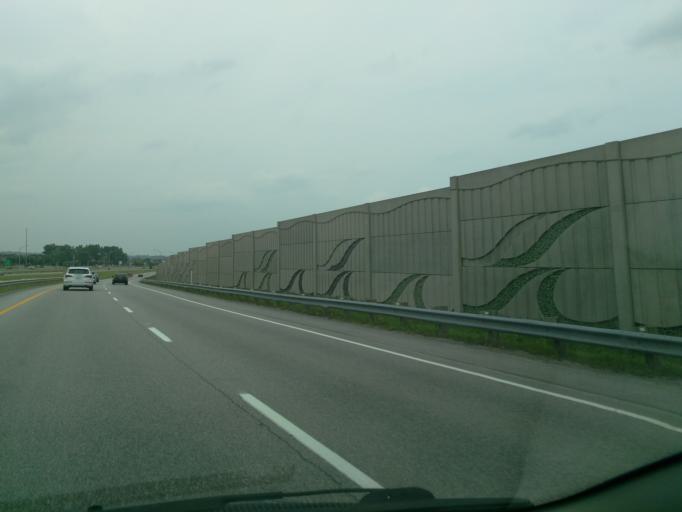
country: CA
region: Quebec
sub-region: Outaouais
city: Gatineau
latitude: 45.4692
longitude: -75.7138
